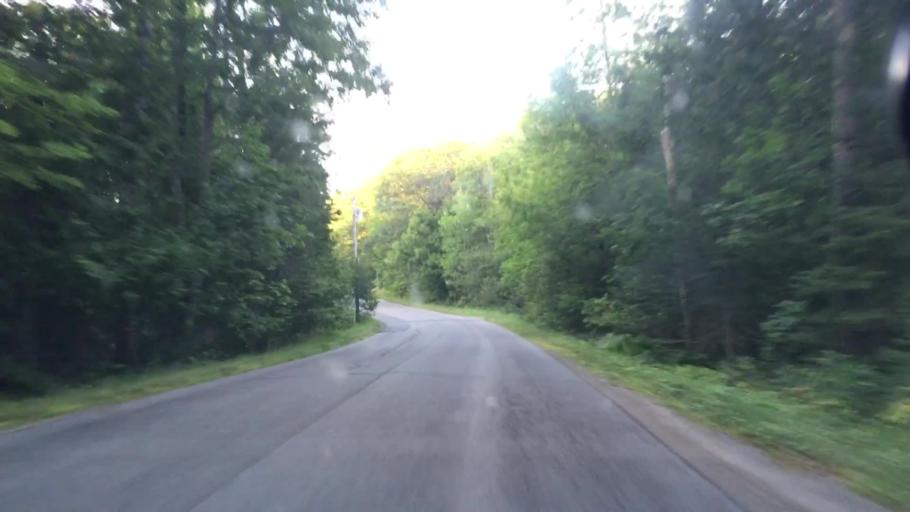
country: US
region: Maine
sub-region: Waldo County
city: Frankfort
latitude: 44.6652
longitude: -68.9265
